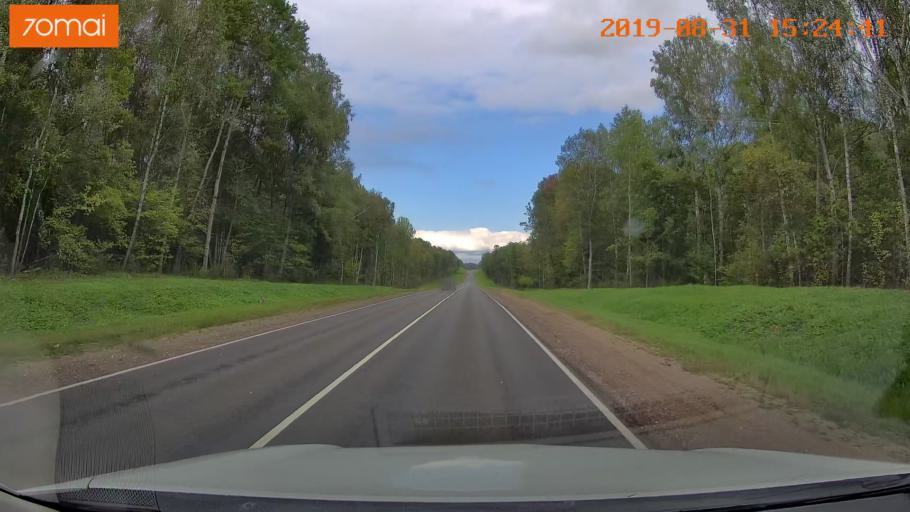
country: RU
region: Kaluga
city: Baryatino
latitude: 54.5311
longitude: 34.5084
